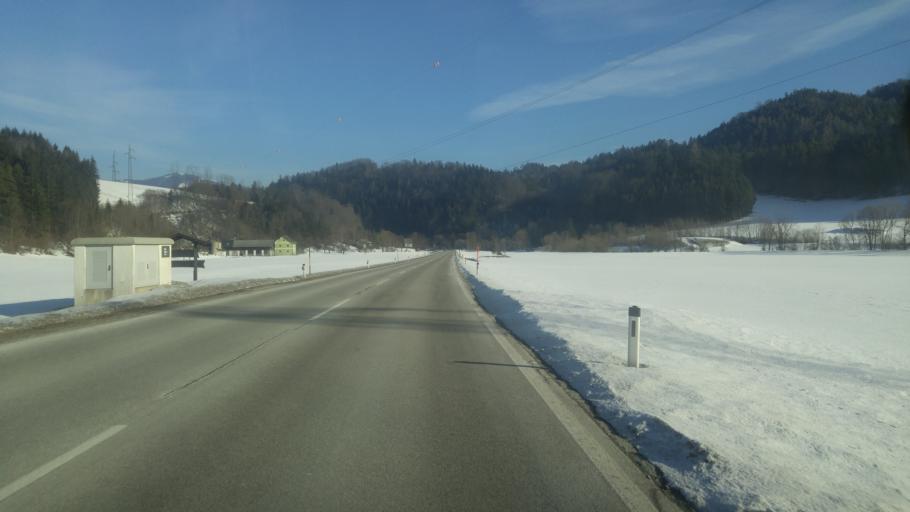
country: AT
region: Lower Austria
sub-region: Politischer Bezirk Lilienfeld
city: Turnitz
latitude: 47.9438
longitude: 15.5088
